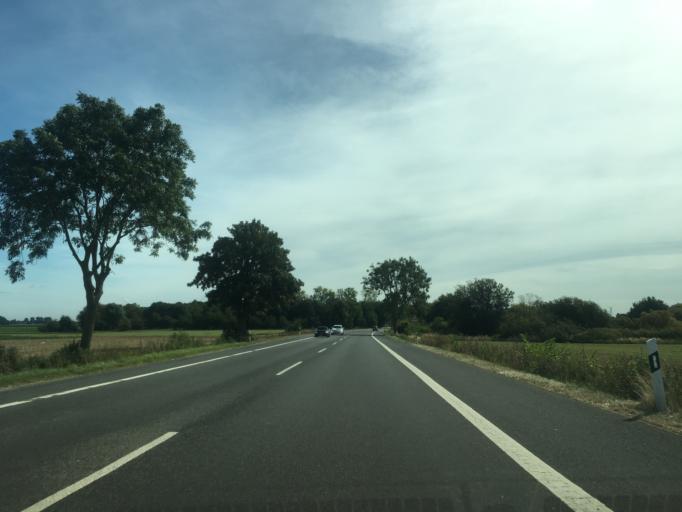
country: DE
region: North Rhine-Westphalia
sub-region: Regierungsbezirk Koln
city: Titz
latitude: 51.0528
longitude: 6.3850
